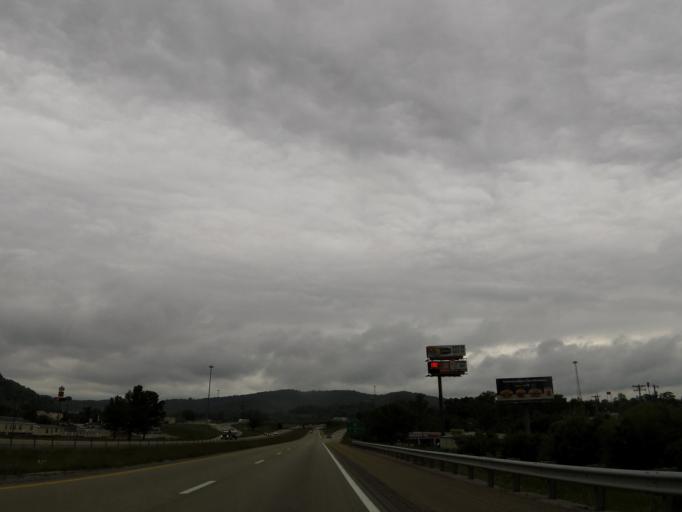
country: US
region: Kentucky
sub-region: Whitley County
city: Williamsburg
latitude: 36.7209
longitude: -84.1620
